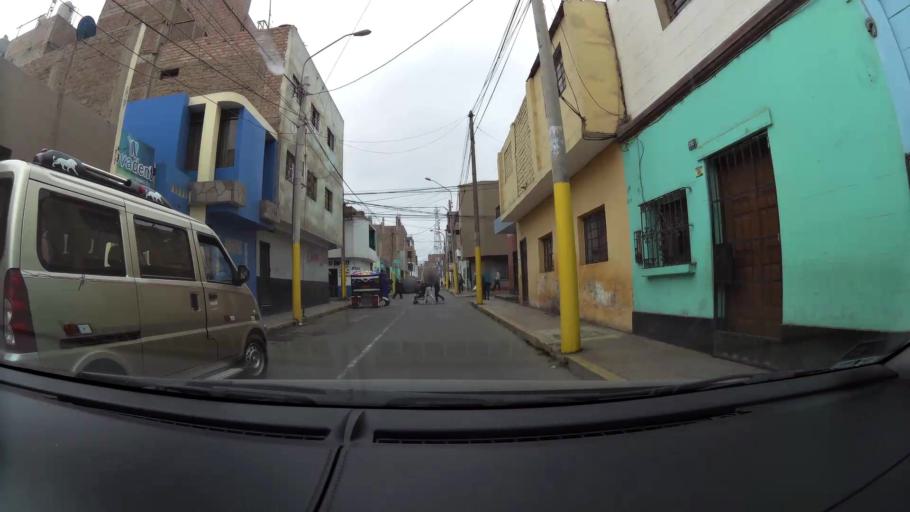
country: PE
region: Lima
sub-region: Provincia de Huaral
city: Huaral
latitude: -11.4966
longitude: -77.2073
